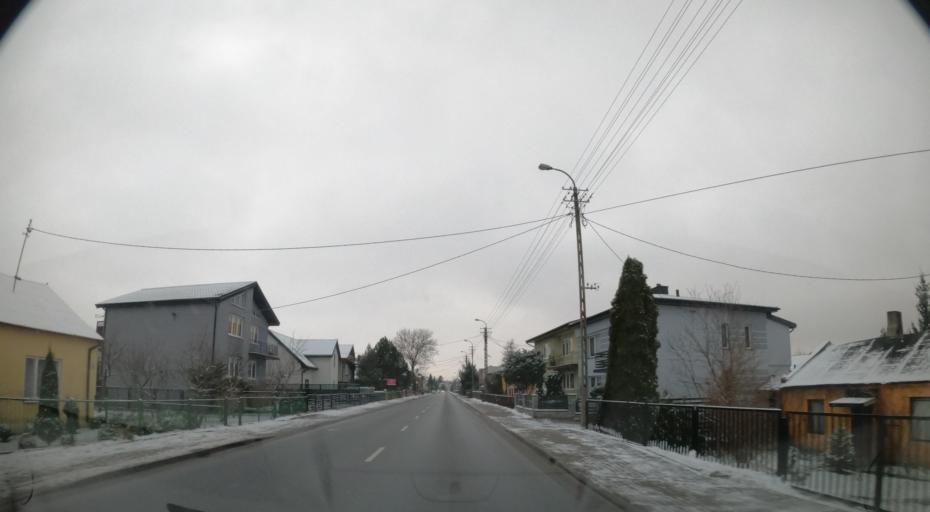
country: PL
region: Kujawsko-Pomorskie
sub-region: Powiat lipnowski
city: Wielgie
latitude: 52.7396
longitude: 19.2701
